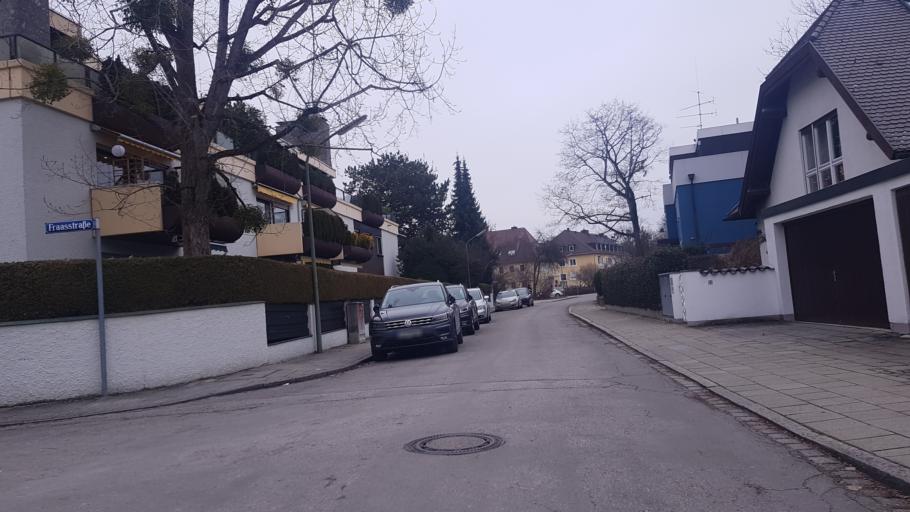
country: DE
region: Bavaria
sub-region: Upper Bavaria
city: Pasing
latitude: 48.1608
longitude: 11.5147
